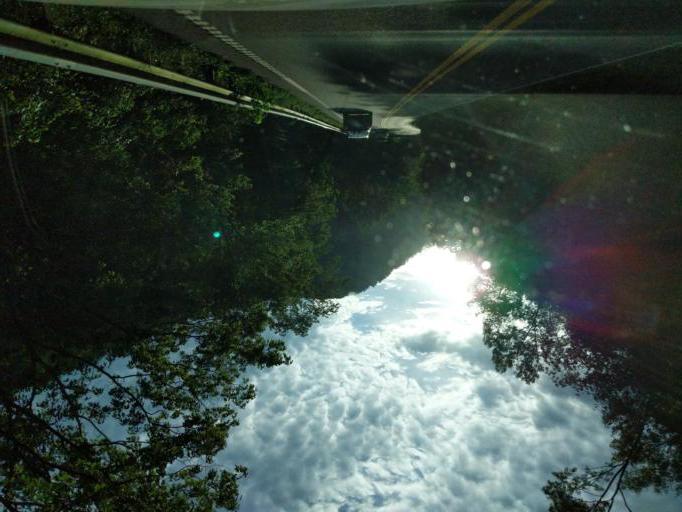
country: US
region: Tennessee
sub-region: Polk County
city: Benton
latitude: 35.0815
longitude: -84.5278
